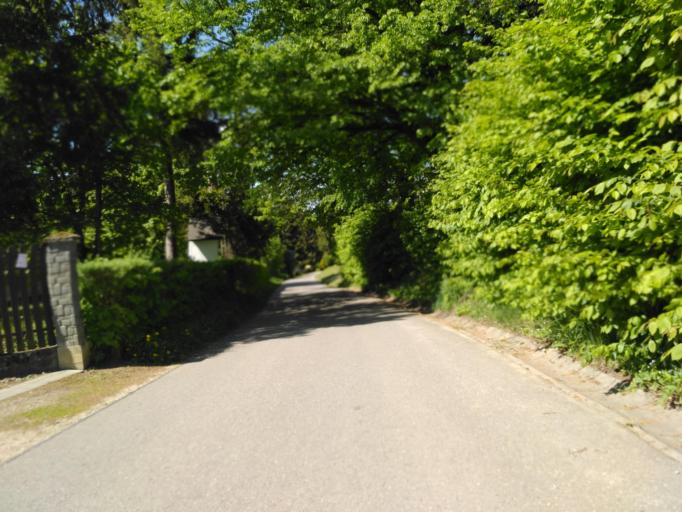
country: PL
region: Subcarpathian Voivodeship
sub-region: Powiat krosnienski
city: Miejsce Piastowe
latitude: 49.6220
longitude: 21.7715
